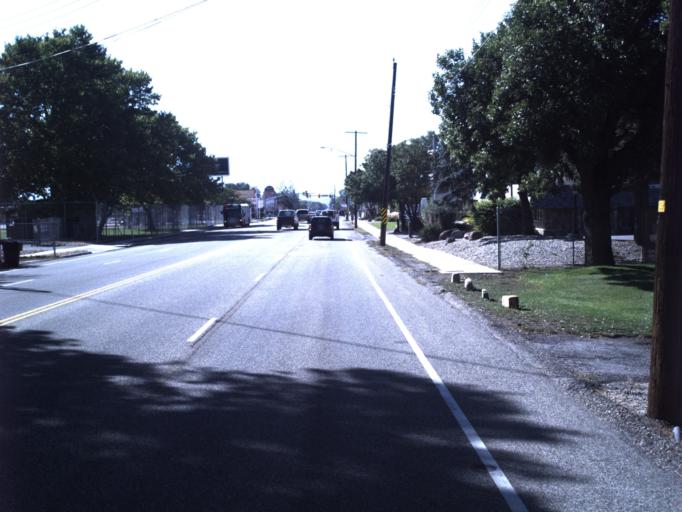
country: US
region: Utah
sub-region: Salt Lake County
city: Canyon Rim
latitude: 40.6999
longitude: -111.8213
